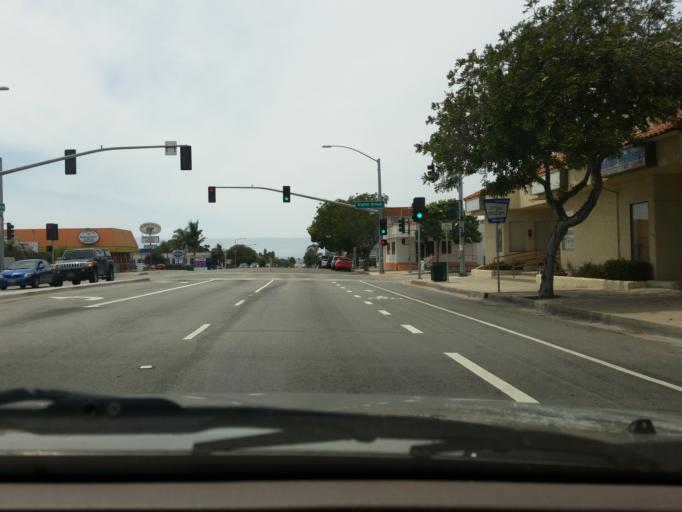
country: US
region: California
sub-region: San Luis Obispo County
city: Grover Beach
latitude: 35.1216
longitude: -120.6209
